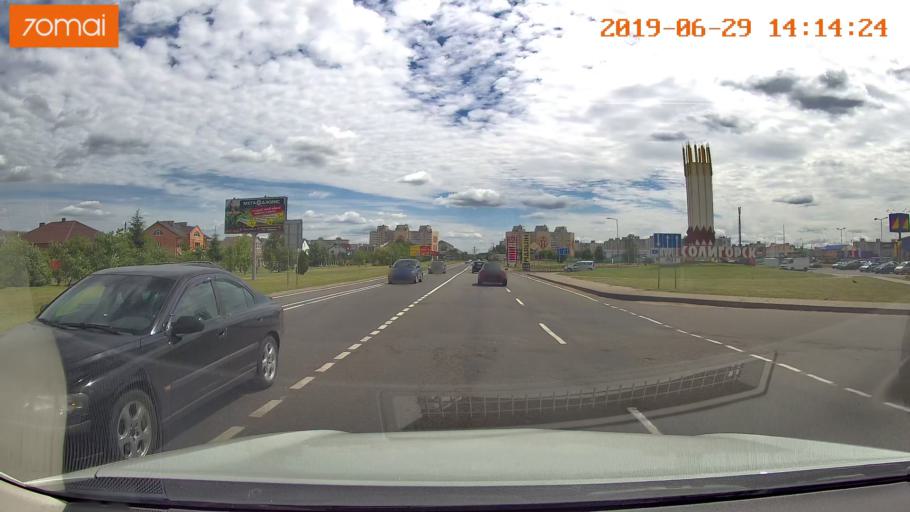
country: BY
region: Minsk
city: Salihorsk
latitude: 52.7960
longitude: 27.5160
